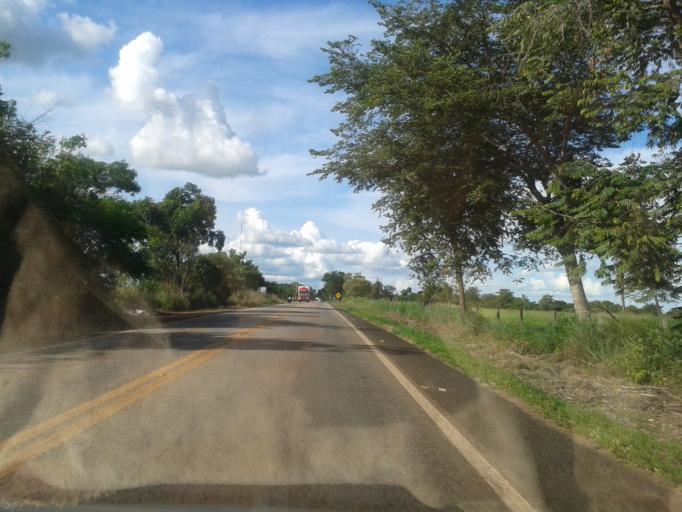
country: BR
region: Goias
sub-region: Mozarlandia
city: Mozarlandia
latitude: -14.6417
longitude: -50.5198
